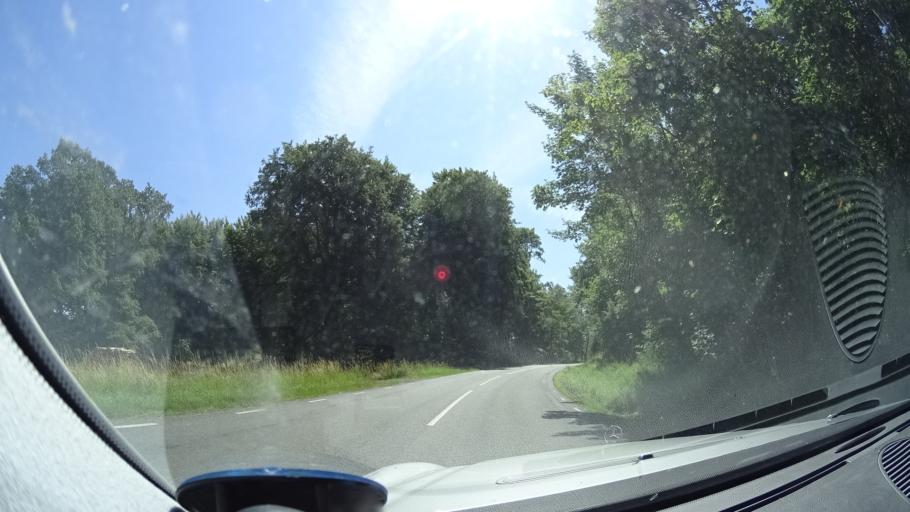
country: SE
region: Skane
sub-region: Kristianstads Kommun
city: Degeberga
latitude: 55.8953
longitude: 14.0032
